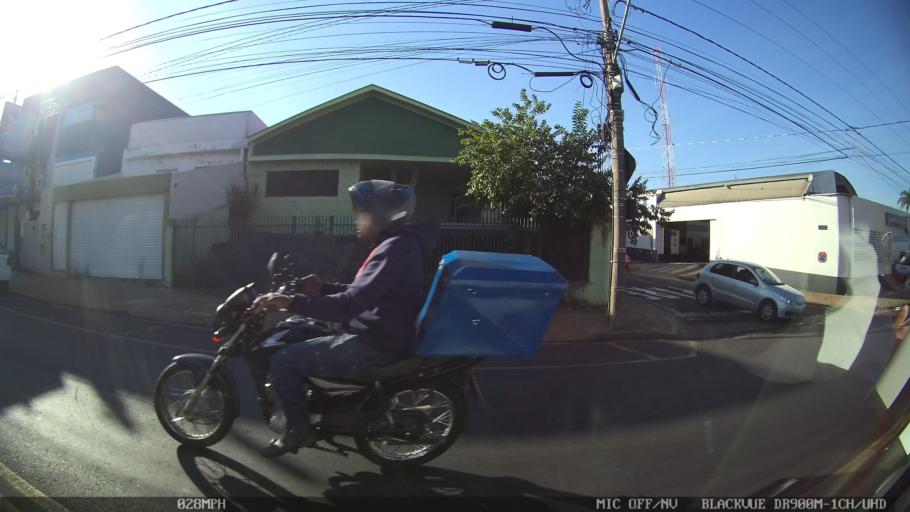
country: BR
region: Sao Paulo
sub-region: Sao Jose Do Rio Preto
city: Sao Jose do Rio Preto
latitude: -20.8110
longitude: -49.3938
